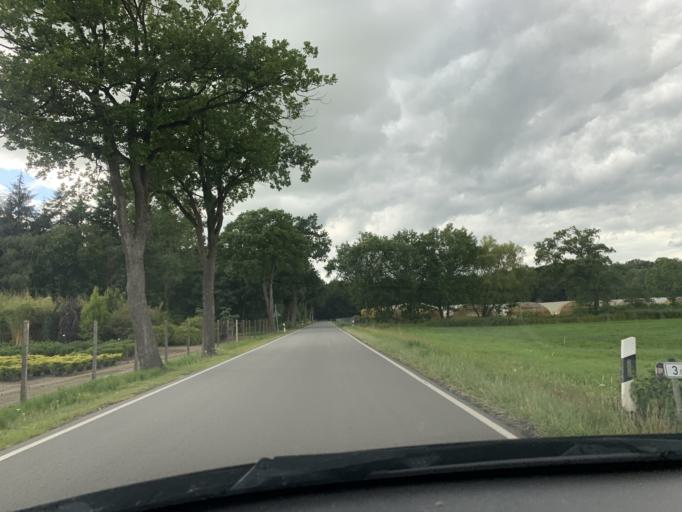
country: DE
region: Lower Saxony
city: Westerstede
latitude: 53.2135
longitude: 7.9257
